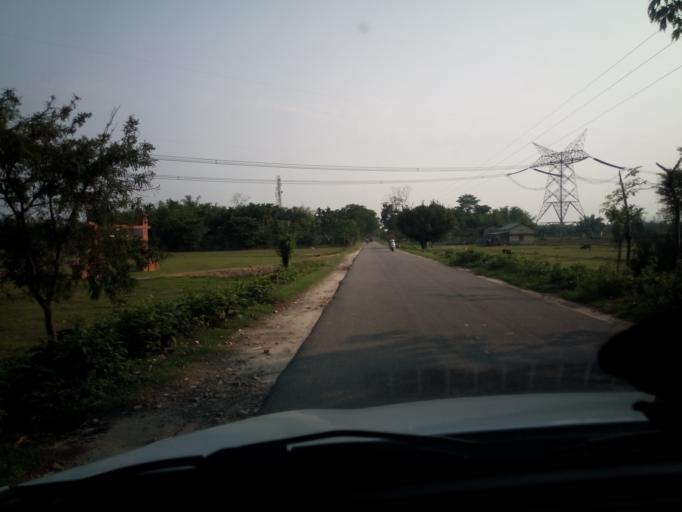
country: IN
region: Assam
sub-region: Udalguri
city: Udalguri
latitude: 26.7152
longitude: 92.0735
